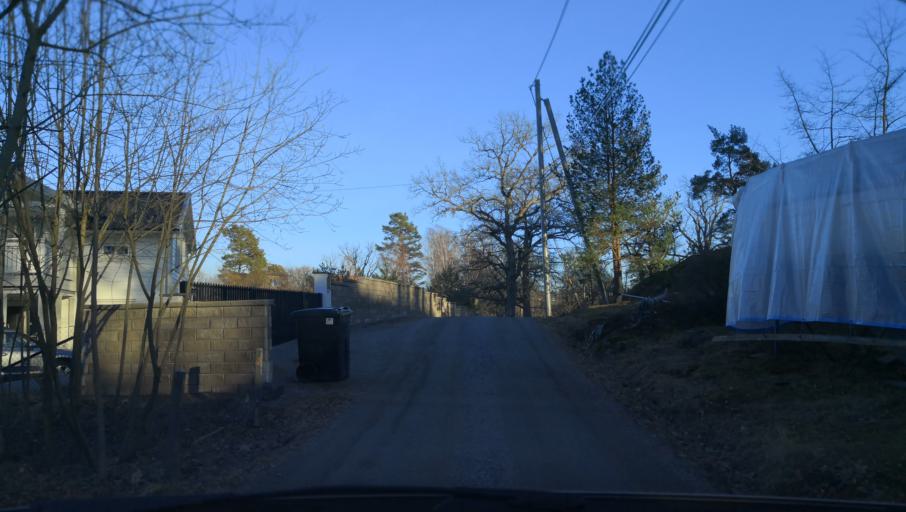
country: SE
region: Stockholm
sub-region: Varmdo Kommun
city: Mortnas
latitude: 59.3283
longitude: 18.4361
